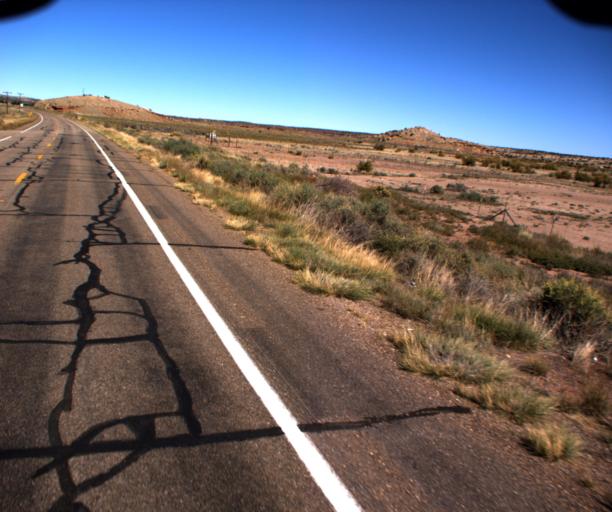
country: US
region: Arizona
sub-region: Apache County
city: Saint Johns
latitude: 34.4149
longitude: -109.4106
